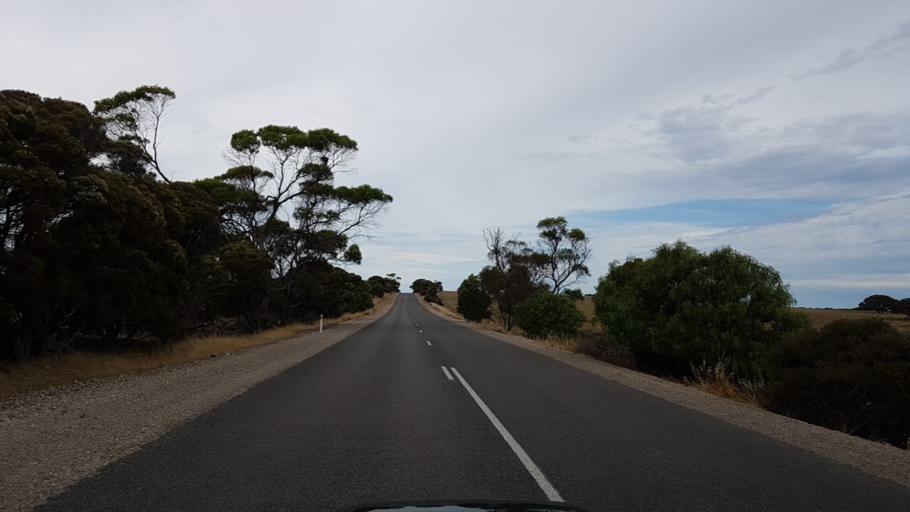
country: AU
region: South Australia
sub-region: Yorke Peninsula
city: Honiton
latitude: -34.9460
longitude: 137.0962
